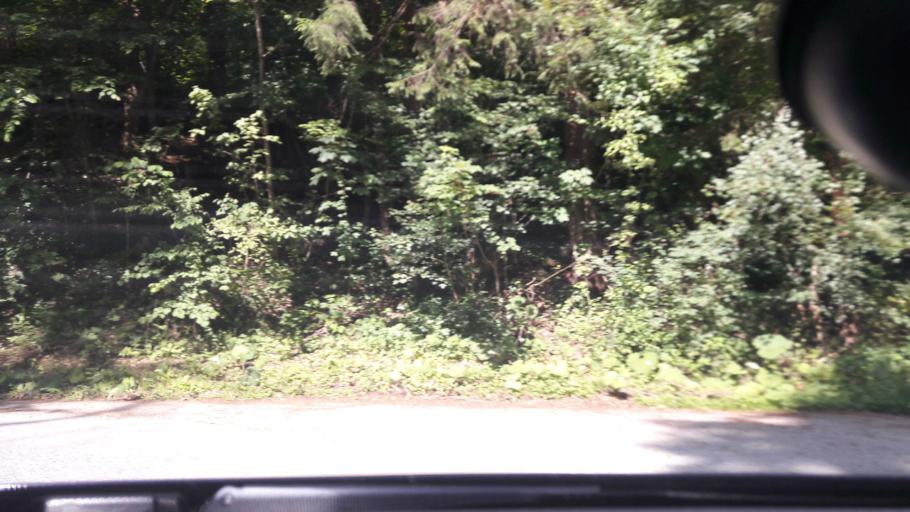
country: AT
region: Styria
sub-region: Politischer Bezirk Voitsberg
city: Sodingberg
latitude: 47.1120
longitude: 15.1882
